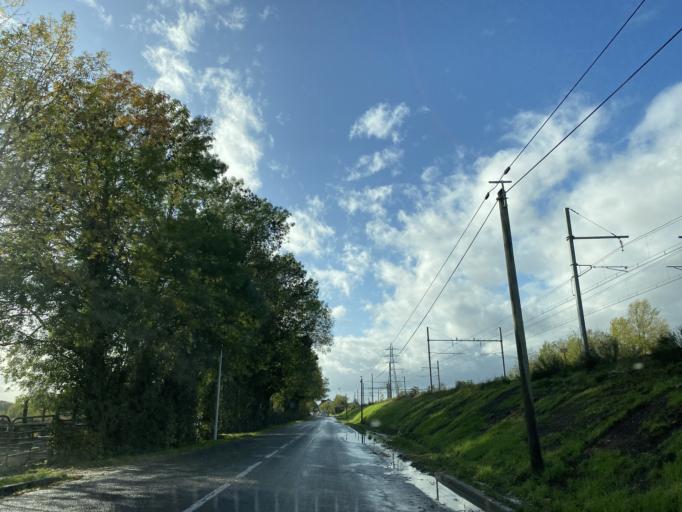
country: FR
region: Centre
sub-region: Departement du Cher
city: Saint-Doulchard
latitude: 47.0947
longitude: 2.3712
